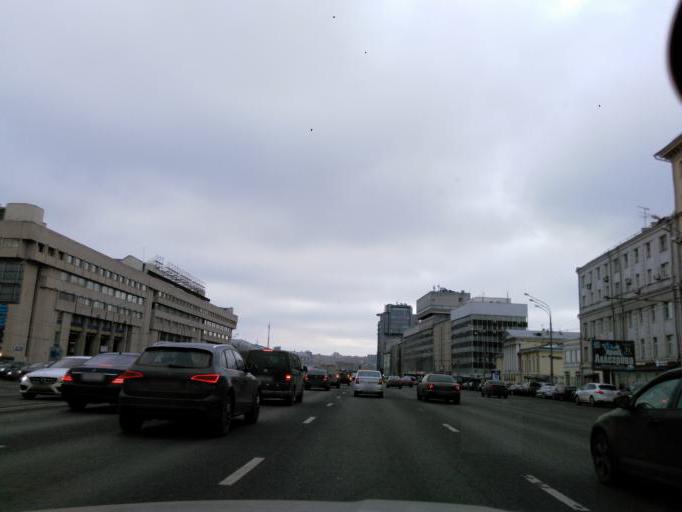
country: RU
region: Moskovskaya
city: Dorogomilovo
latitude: 55.7379
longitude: 37.5875
